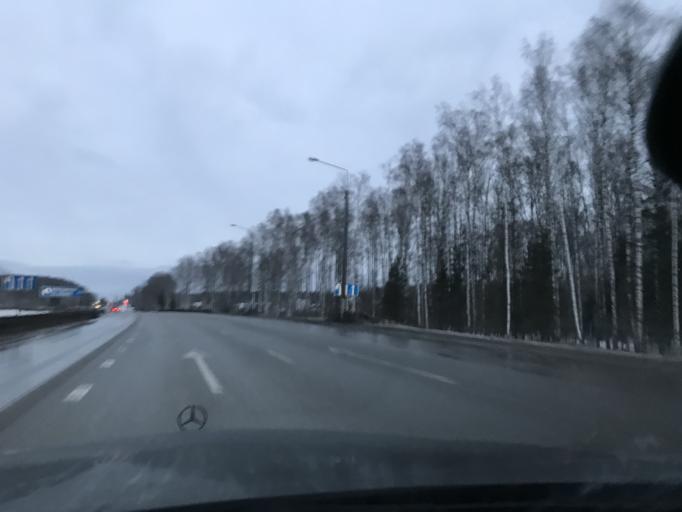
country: RU
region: Vladimir
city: Petushki
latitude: 55.9453
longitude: 39.5138
